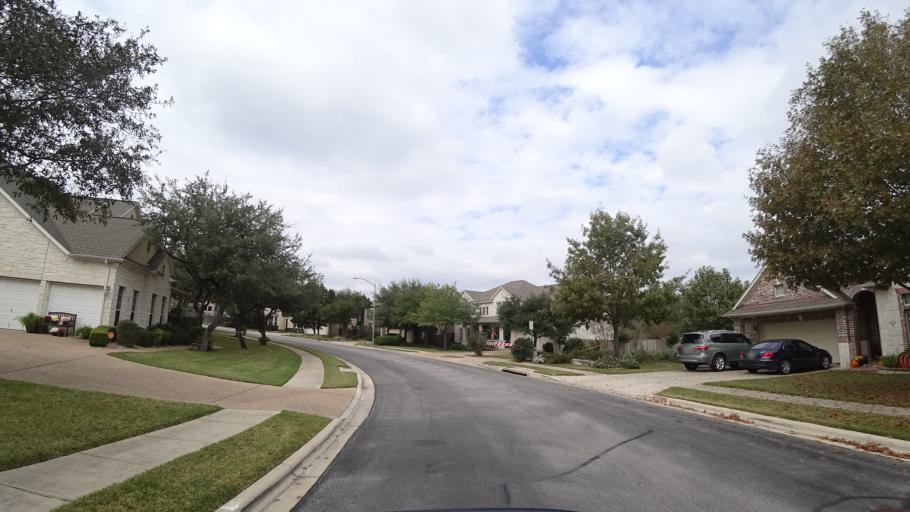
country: US
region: Texas
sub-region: Travis County
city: Shady Hollow
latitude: 30.2165
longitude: -97.8836
